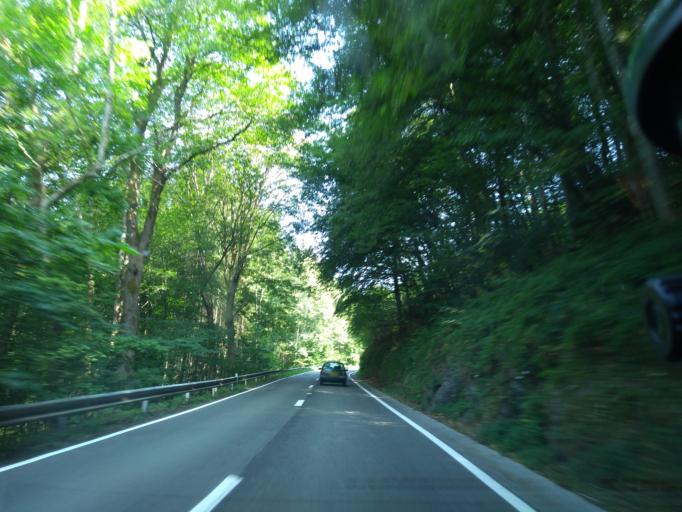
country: BE
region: Wallonia
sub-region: Province du Luxembourg
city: La Roche-en-Ardenne
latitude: 50.1790
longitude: 5.6444
